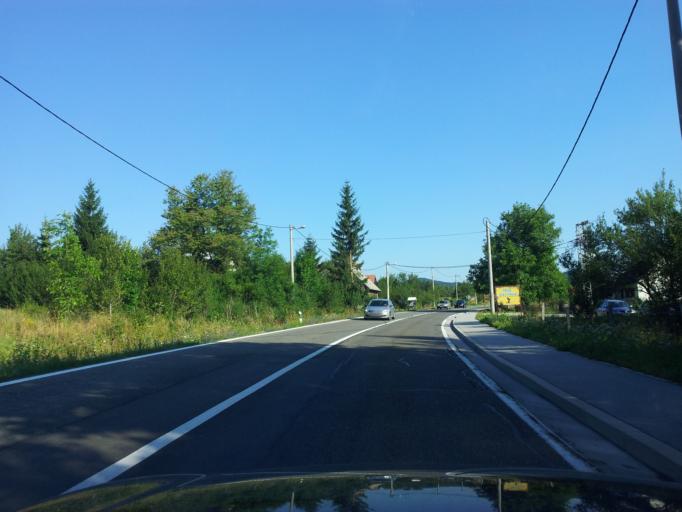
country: HR
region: Licko-Senjska
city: Jezerce
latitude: 44.7606
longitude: 15.6931
